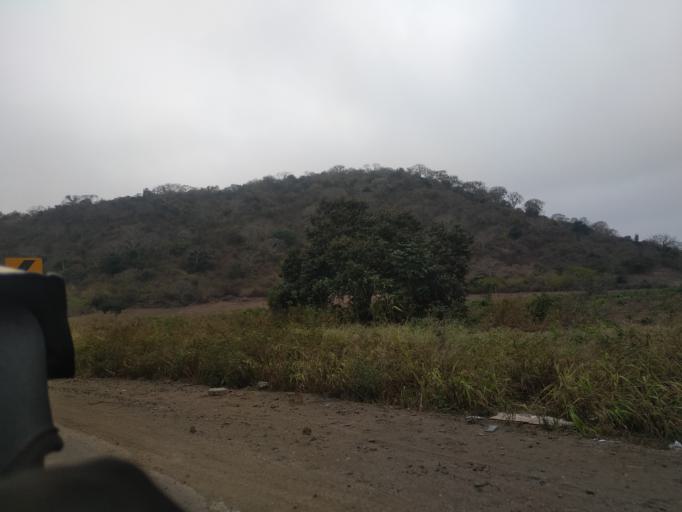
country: EC
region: Manabi
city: Montecristi
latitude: -1.0876
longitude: -80.6887
